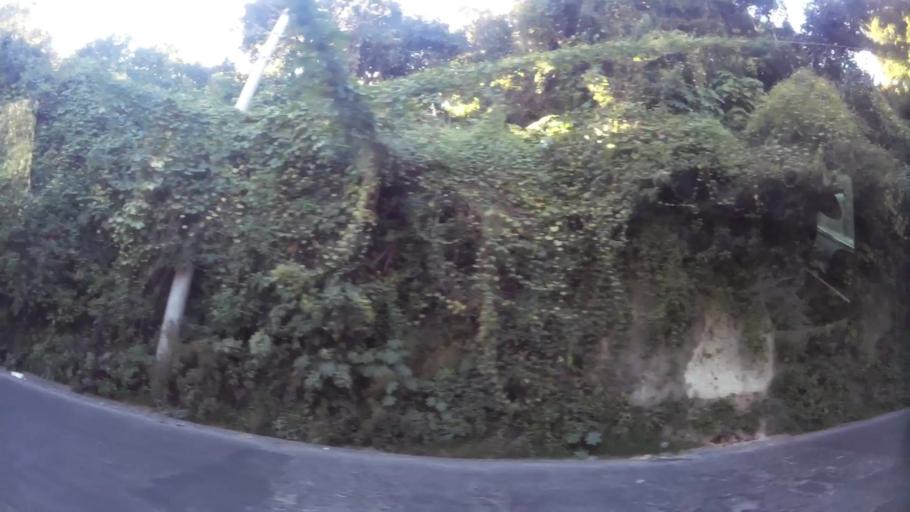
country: GT
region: Guatemala
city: Villa Nueva
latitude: 14.5518
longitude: -90.6220
